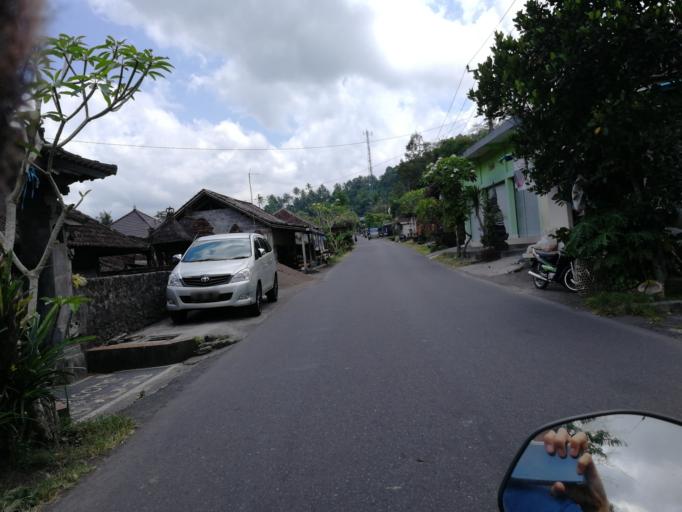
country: ID
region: Bali
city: Banjar Wangsian
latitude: -8.4575
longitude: 115.4501
